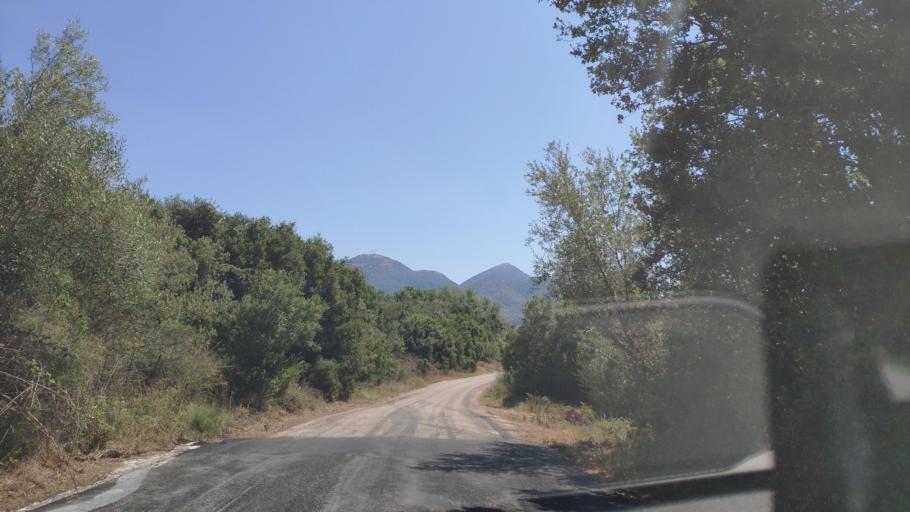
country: GR
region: Epirus
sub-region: Nomos Prevezis
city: Kanalaki
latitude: 39.2727
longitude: 20.6000
